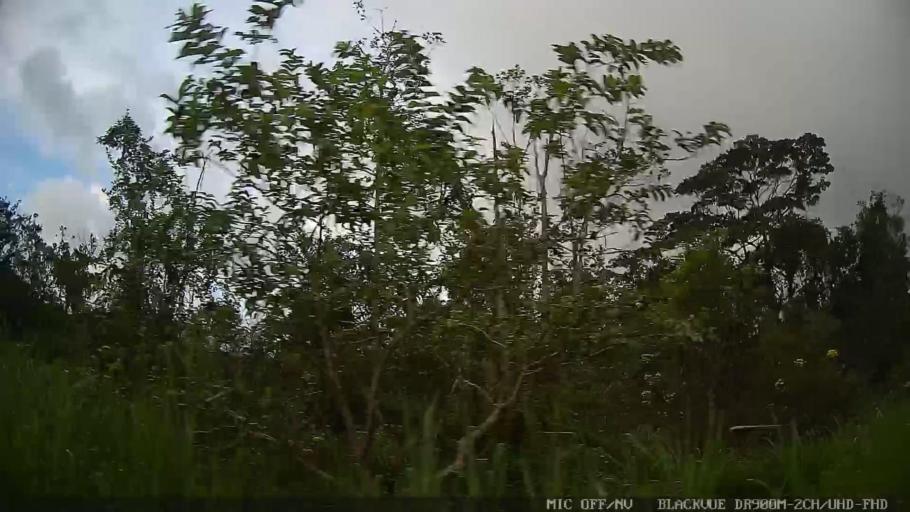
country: BR
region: Sao Paulo
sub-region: Itanhaem
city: Itanhaem
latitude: -24.1178
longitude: -46.7868
